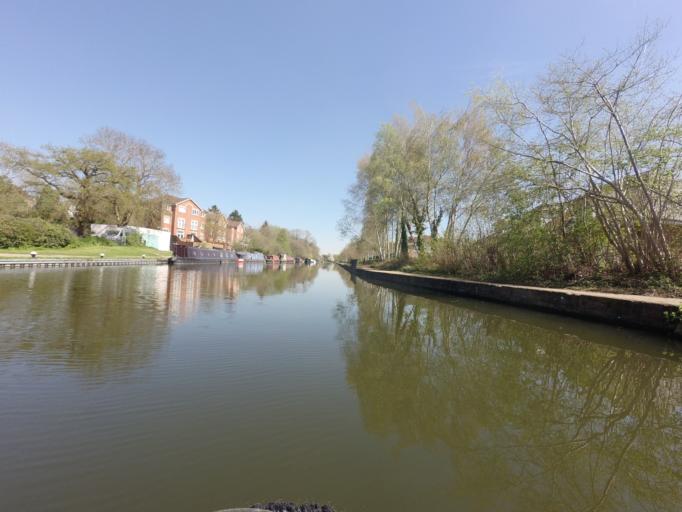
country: GB
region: England
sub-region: Hertfordshire
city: Rickmansworth
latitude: 51.6454
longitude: -0.4385
